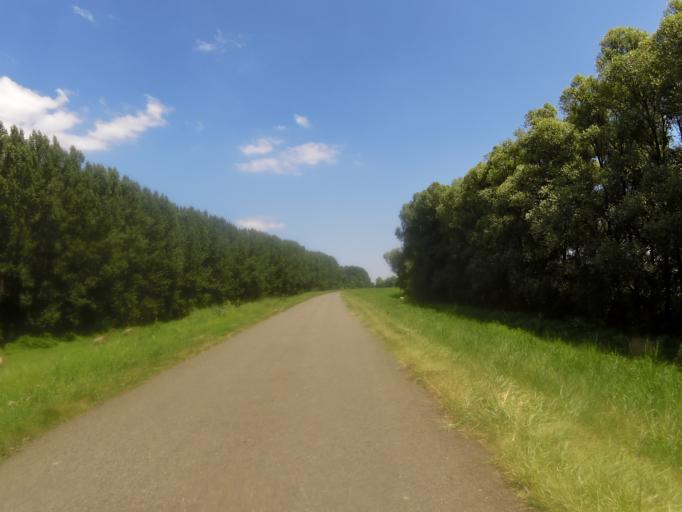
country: HU
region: Jasz-Nagykun-Szolnok
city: Abadszalok
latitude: 47.5294
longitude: 20.5942
